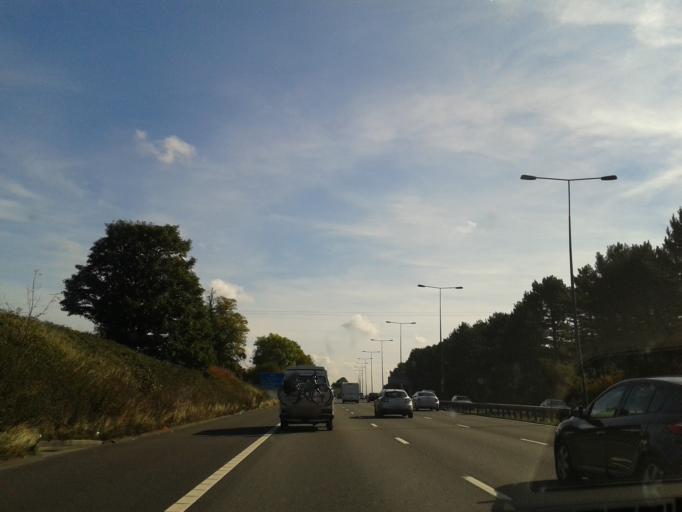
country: GB
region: England
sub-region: Staffordshire
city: Newcastle under Lyme
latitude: 52.9927
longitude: -2.2793
